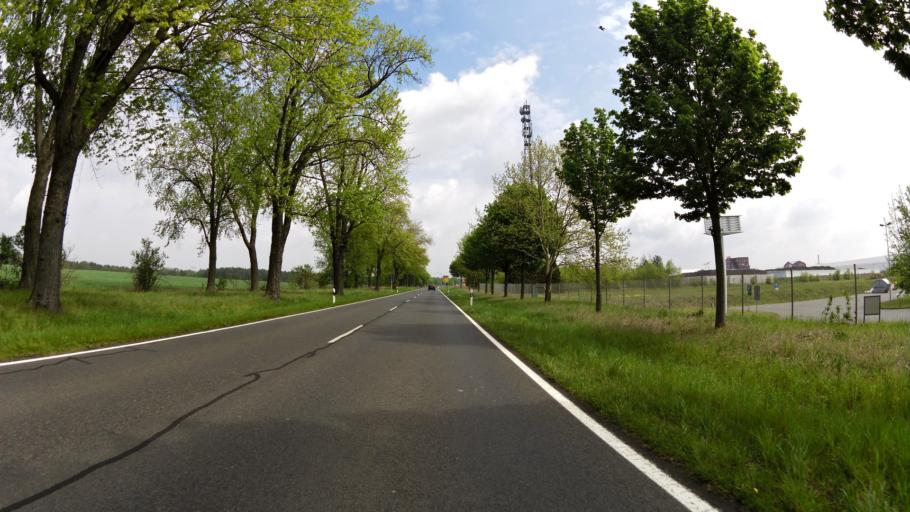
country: DE
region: Brandenburg
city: Mittenwalde
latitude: 52.2625
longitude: 13.5682
